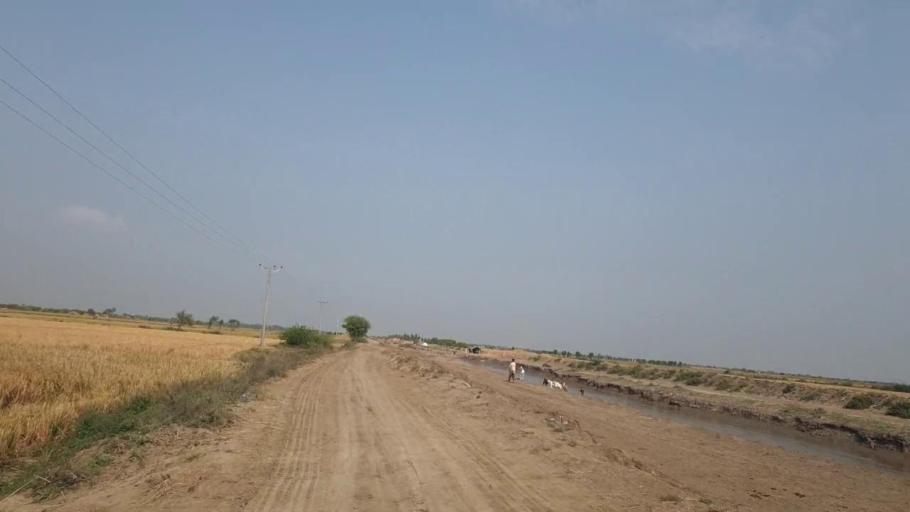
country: PK
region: Sindh
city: Badin
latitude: 24.7399
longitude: 68.7650
